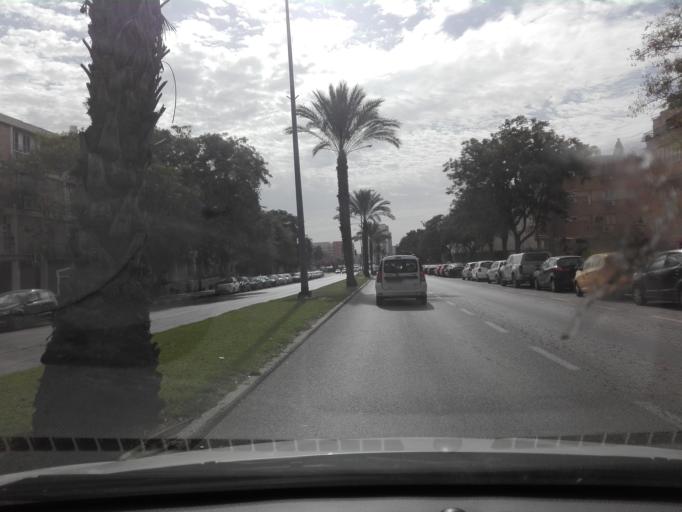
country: IL
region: Southern District
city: Beersheba
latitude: 31.2655
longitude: 34.7981
